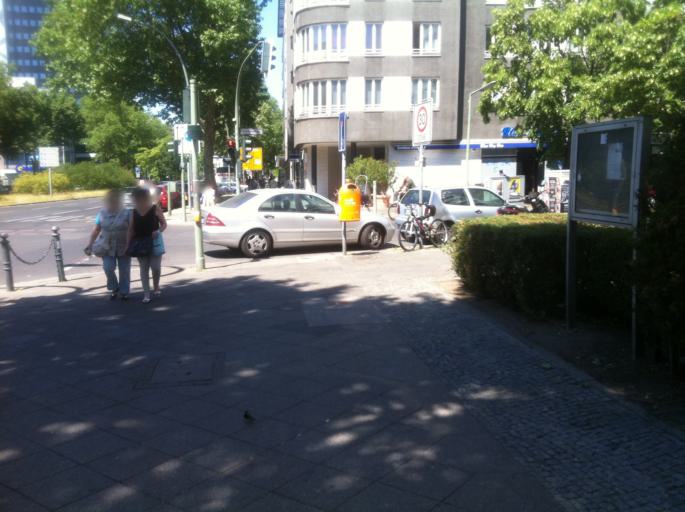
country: DE
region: Berlin
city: Berlin Schoeneberg
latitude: 52.5003
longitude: 13.3503
